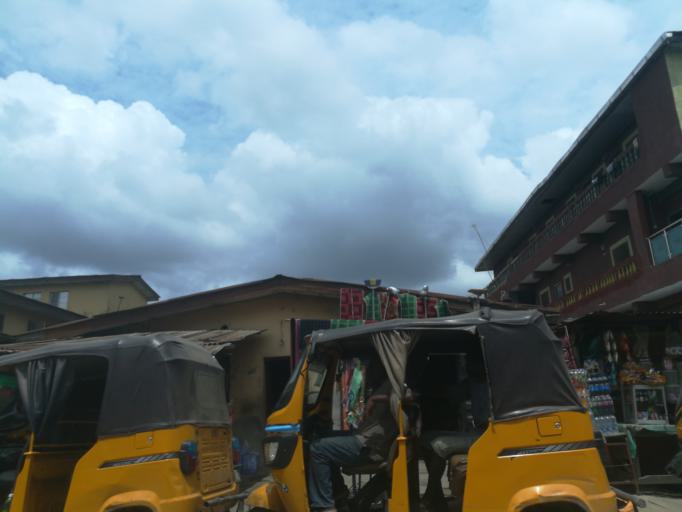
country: NG
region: Lagos
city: Somolu
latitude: 6.5357
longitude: 3.3918
